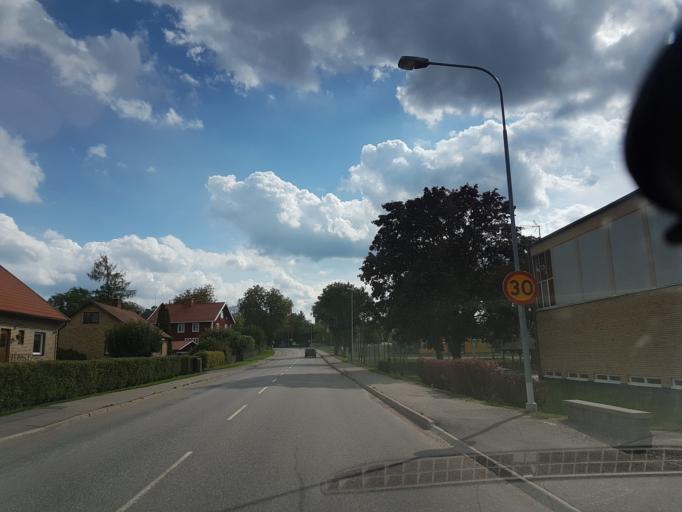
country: SE
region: OEstergoetland
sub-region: Linkopings Kommun
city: Vikingstad
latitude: 58.3811
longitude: 15.4369
